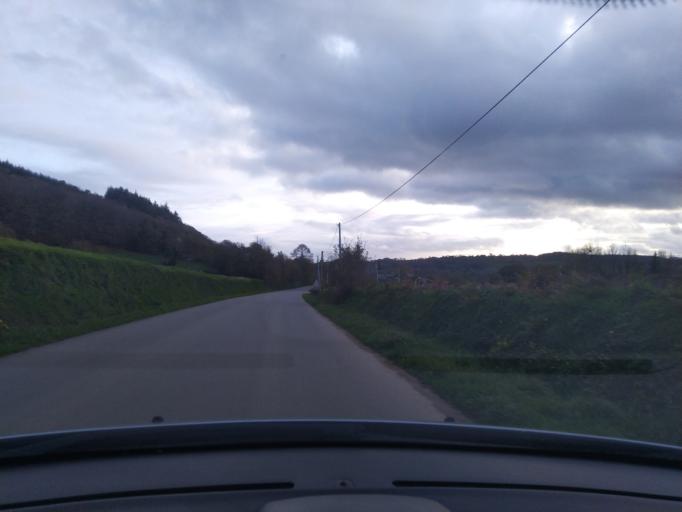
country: FR
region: Brittany
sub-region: Departement du Finistere
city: Guerlesquin
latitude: 48.5491
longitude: -3.6198
